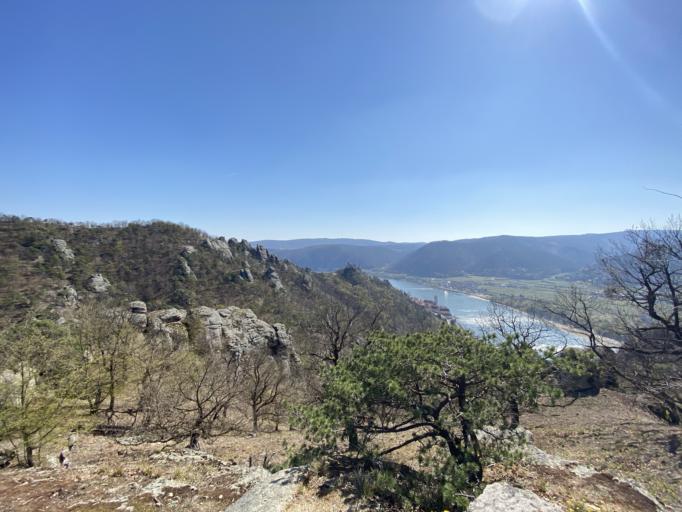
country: AT
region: Lower Austria
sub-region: Politischer Bezirk Krems
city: Durnstein
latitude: 48.4031
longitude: 15.5211
